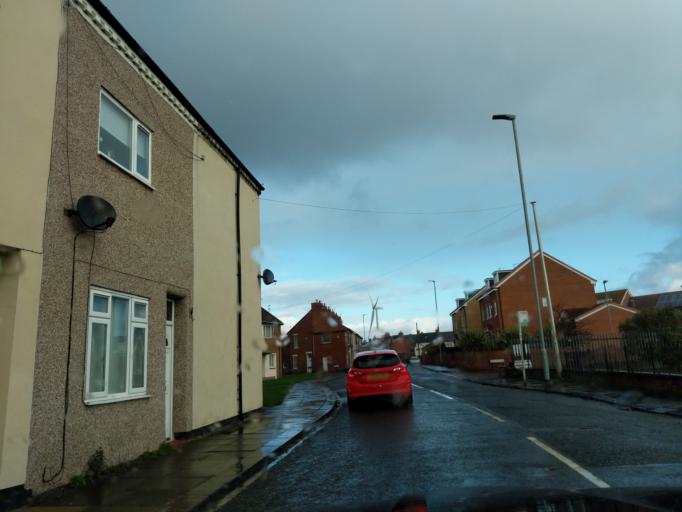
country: GB
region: England
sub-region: Northumberland
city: Blyth
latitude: 55.1228
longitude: -1.5066
